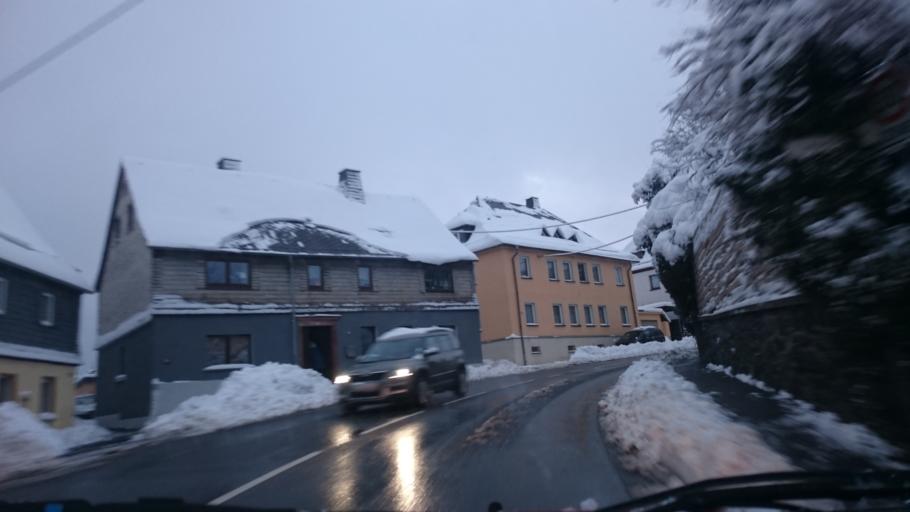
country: DE
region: Saxony
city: Hartenstein
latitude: 50.6636
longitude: 12.6656
